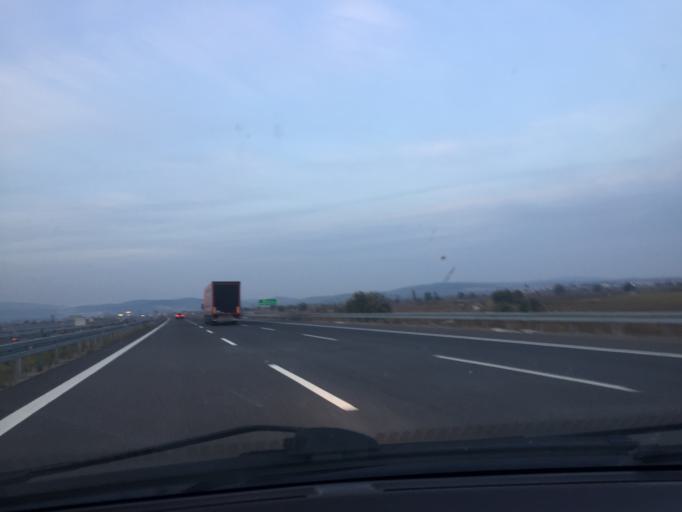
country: TR
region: Manisa
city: Halitpasa
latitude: 38.7438
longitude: 27.6589
